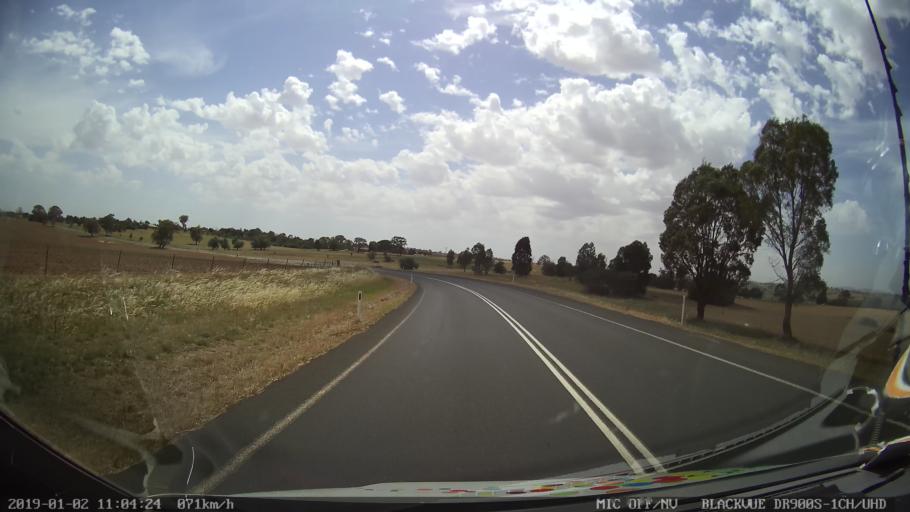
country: AU
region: New South Wales
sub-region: Young
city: Young
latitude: -34.5750
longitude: 148.3521
